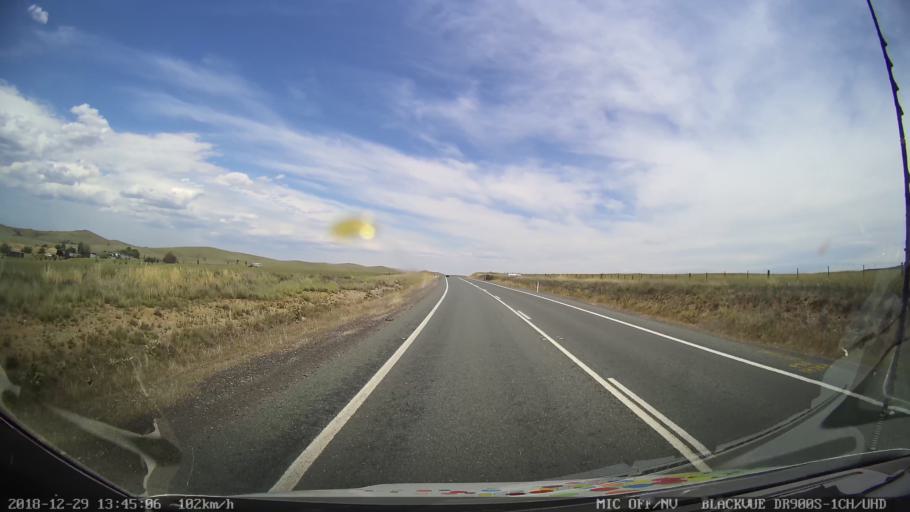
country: AU
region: New South Wales
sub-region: Cooma-Monaro
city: Cooma
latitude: -36.0913
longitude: 149.1452
